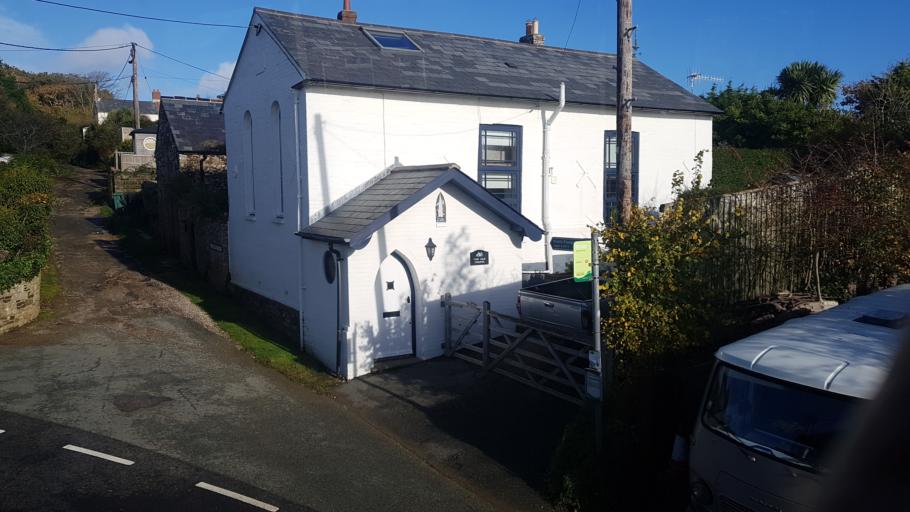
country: GB
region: England
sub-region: Isle of Wight
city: Shalfleet
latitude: 50.6459
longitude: -1.4065
